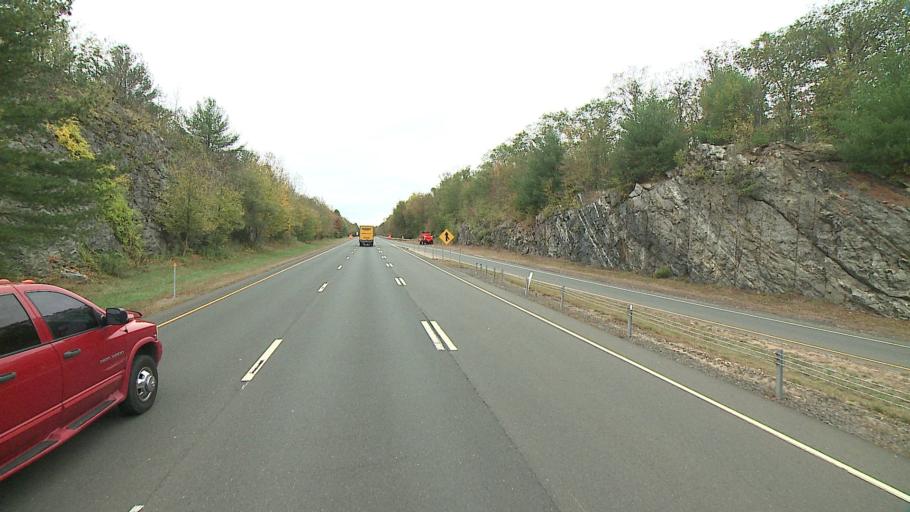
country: US
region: Connecticut
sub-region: Middlesex County
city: Higganum
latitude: 41.4578
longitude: -72.5293
